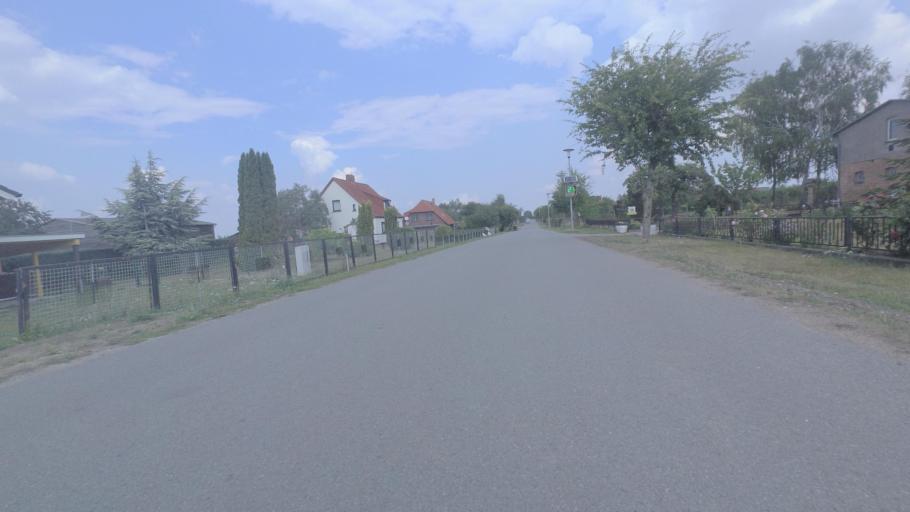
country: DE
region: Mecklenburg-Vorpommern
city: Borrentin
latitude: 53.7860
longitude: 12.8778
